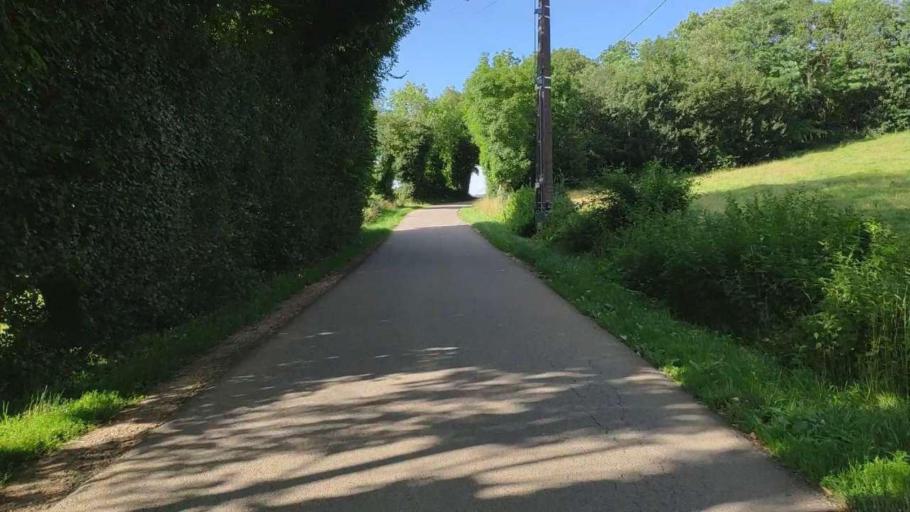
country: FR
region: Franche-Comte
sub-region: Departement du Jura
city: Bletterans
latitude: 46.7534
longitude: 5.5251
